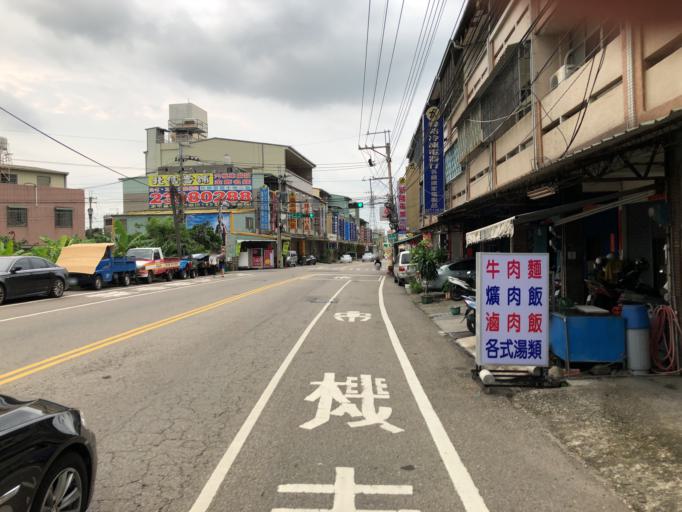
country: TW
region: Taiwan
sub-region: Taichung City
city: Taichung
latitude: 24.0959
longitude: 120.7289
